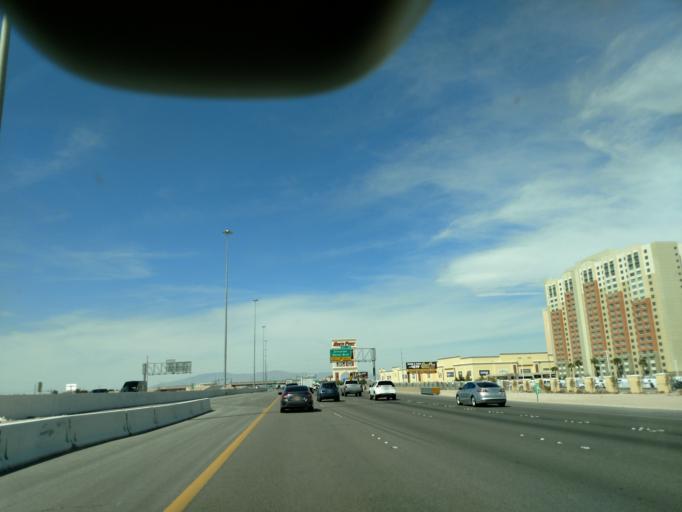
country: US
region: Nevada
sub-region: Clark County
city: Enterprise
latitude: 36.0065
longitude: -115.1804
